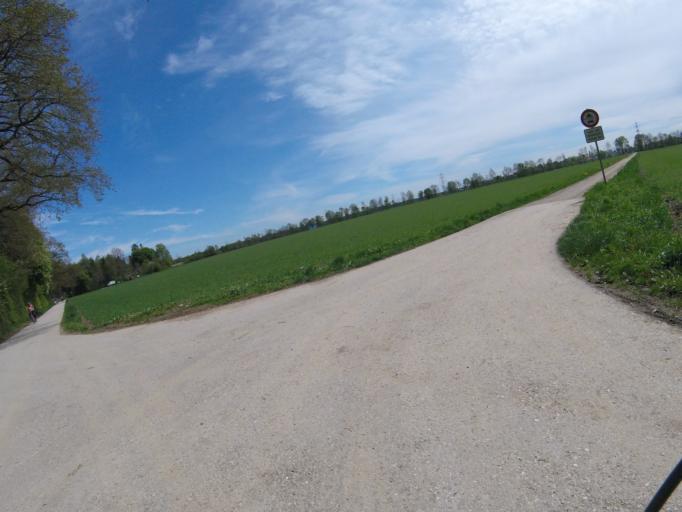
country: DE
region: Bavaria
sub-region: Upper Bavaria
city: Hohenbrunn
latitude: 48.0577
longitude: 11.6914
